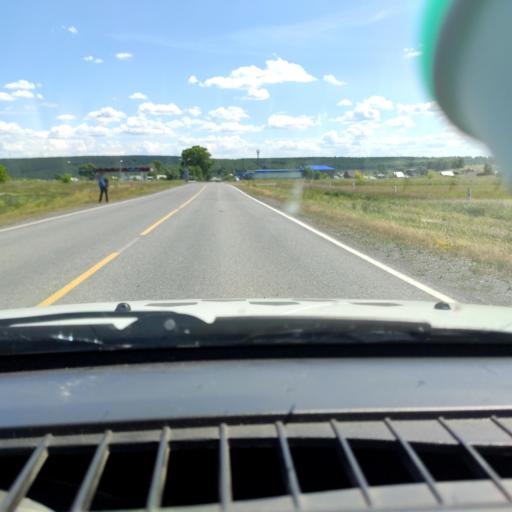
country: RU
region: Chelyabinsk
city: Mezhevoy
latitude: 55.2324
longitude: 58.8171
